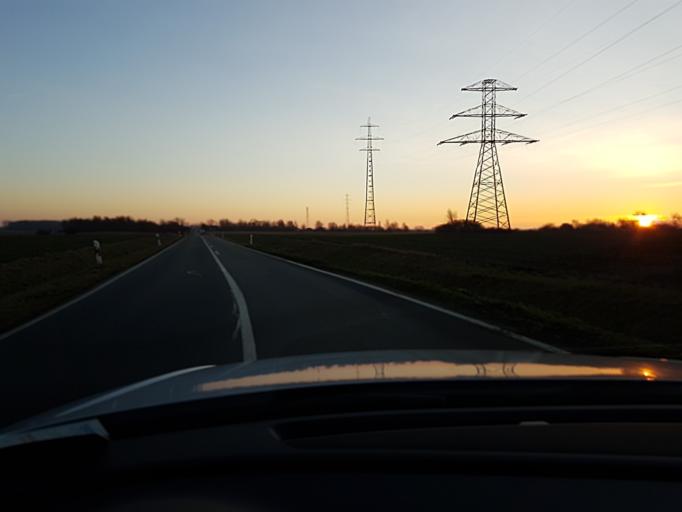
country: DE
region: Mecklenburg-Vorpommern
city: Wiek
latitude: 54.5642
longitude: 13.2476
